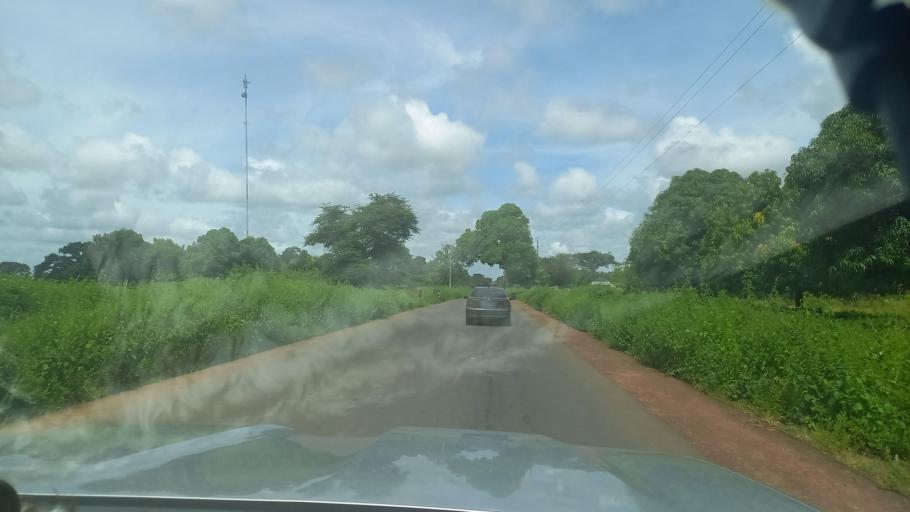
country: GM
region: Lower River
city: Kaiaf
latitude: 13.2063
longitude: -15.5485
